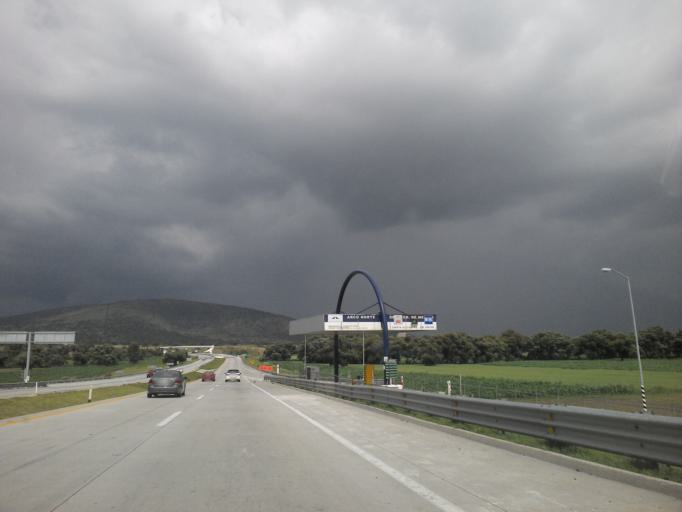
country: MX
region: Mexico
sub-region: Hueypoxtla
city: Santa Maria Ajoloapan
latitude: 19.9557
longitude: -99.0533
